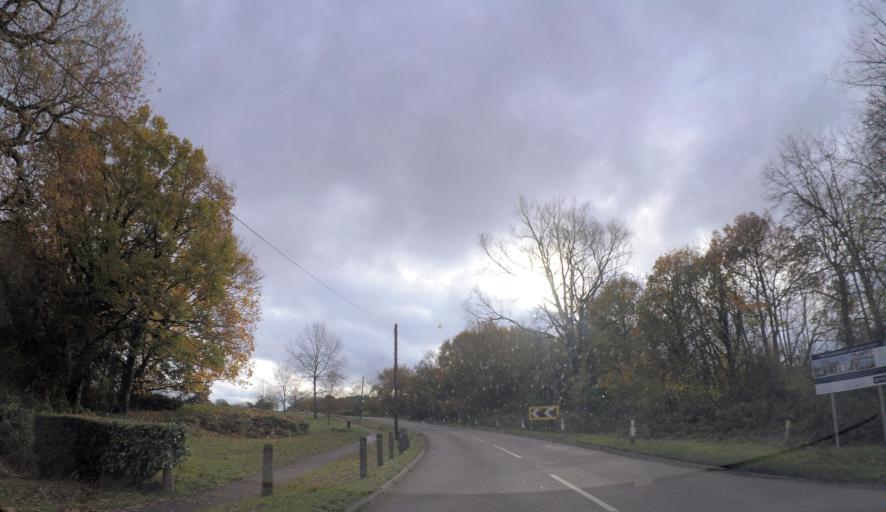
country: GB
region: England
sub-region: Surrey
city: Salfords
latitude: 51.2132
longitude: -0.1753
